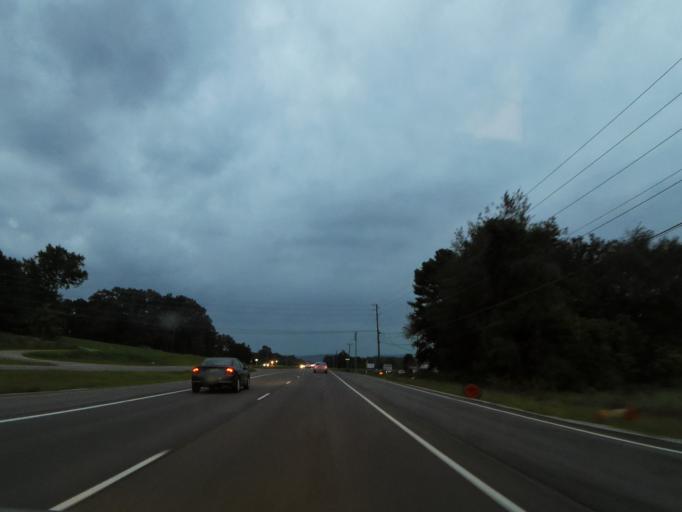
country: US
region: Alabama
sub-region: Madison County
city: Moores Mill
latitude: 34.7498
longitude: -86.4577
